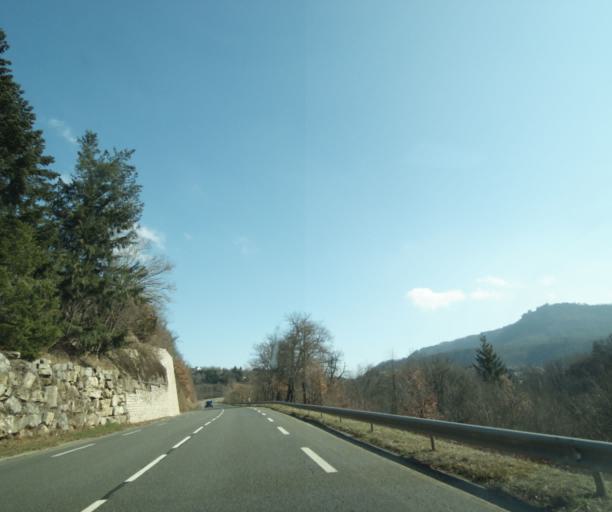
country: FR
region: Languedoc-Roussillon
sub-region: Departement de la Lozere
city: Mende
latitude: 44.5370
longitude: 3.5326
